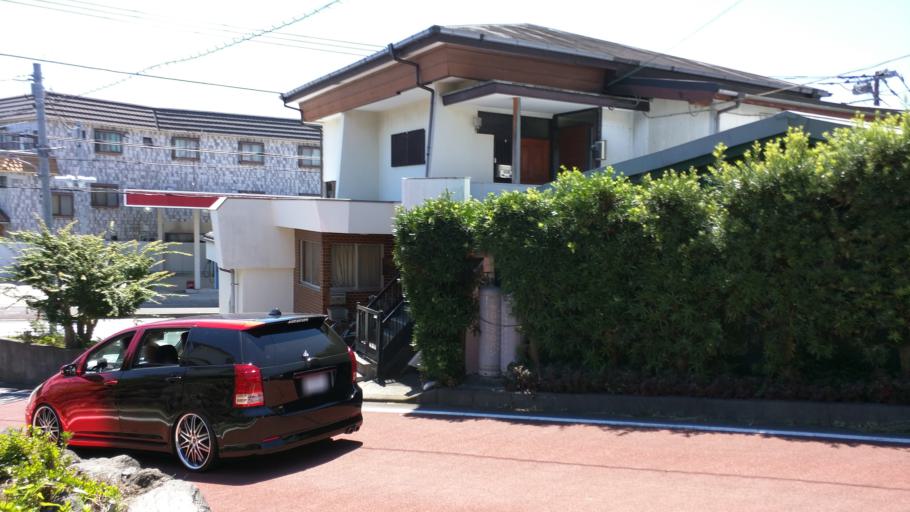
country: JP
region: Shizuoka
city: Ito
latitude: 34.8868
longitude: 139.1205
